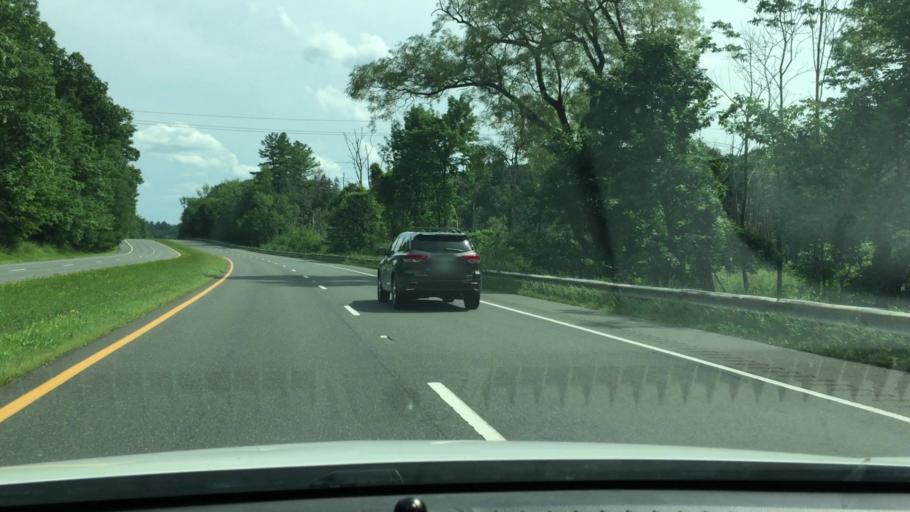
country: US
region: Massachusetts
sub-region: Berkshire County
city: Lenox
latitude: 42.3683
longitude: -73.2774
